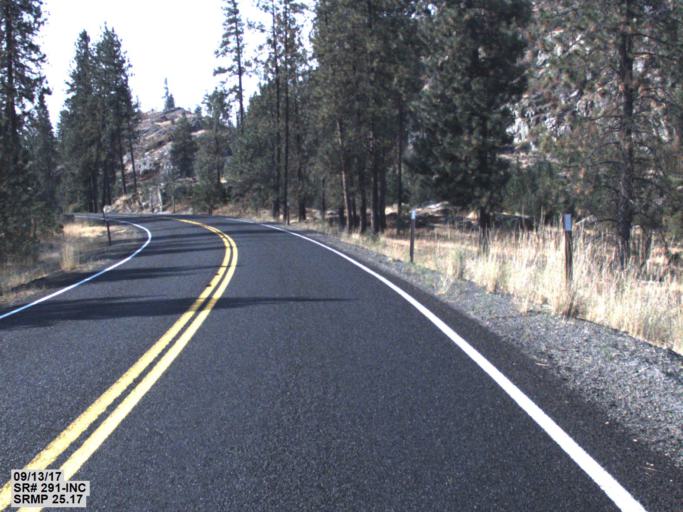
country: US
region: Washington
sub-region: Spokane County
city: Airway Heights
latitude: 47.8635
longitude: -117.7118
